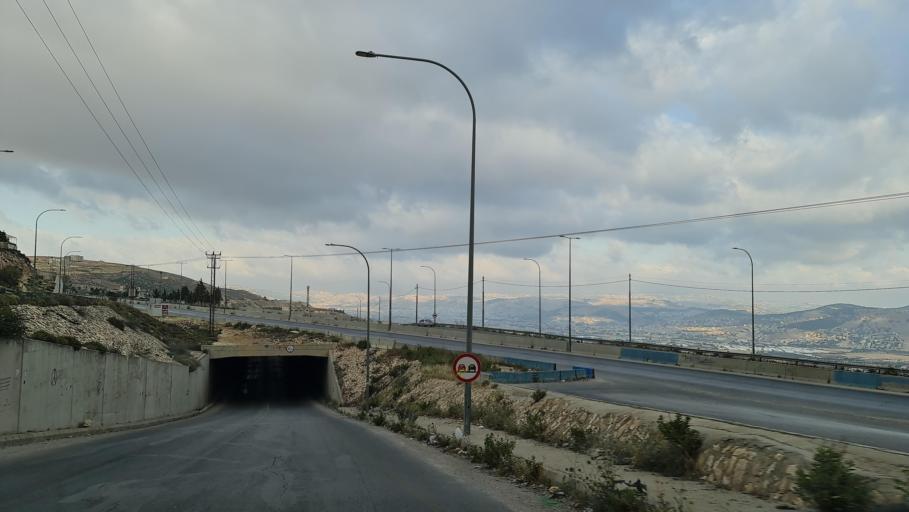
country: JO
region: Amman
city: Al Jubayhah
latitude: 32.0928
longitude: 35.8972
